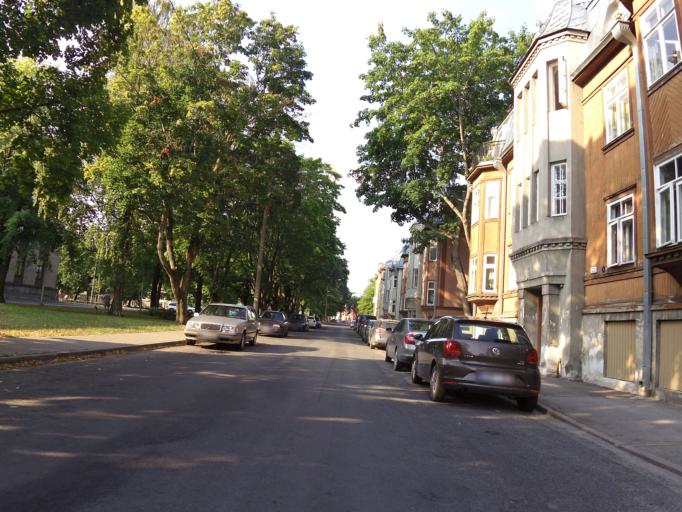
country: EE
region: Harju
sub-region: Tallinna linn
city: Tallinn
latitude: 59.4454
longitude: 24.7291
